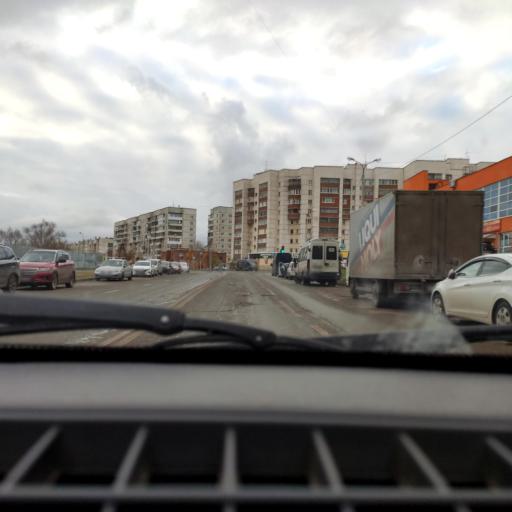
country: RU
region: Bashkortostan
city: Mikhaylovka
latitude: 54.7116
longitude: 55.8356
